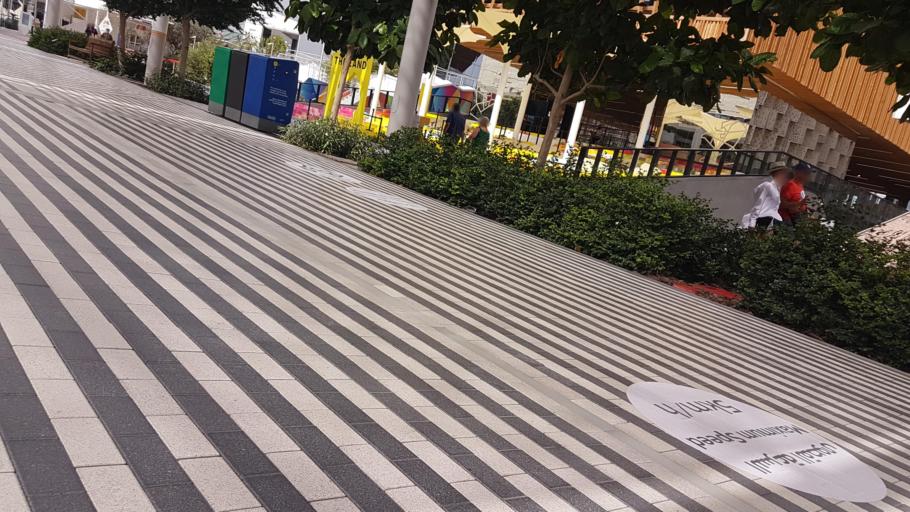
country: AE
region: Dubai
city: Dubai
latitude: 24.9649
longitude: 55.1512
